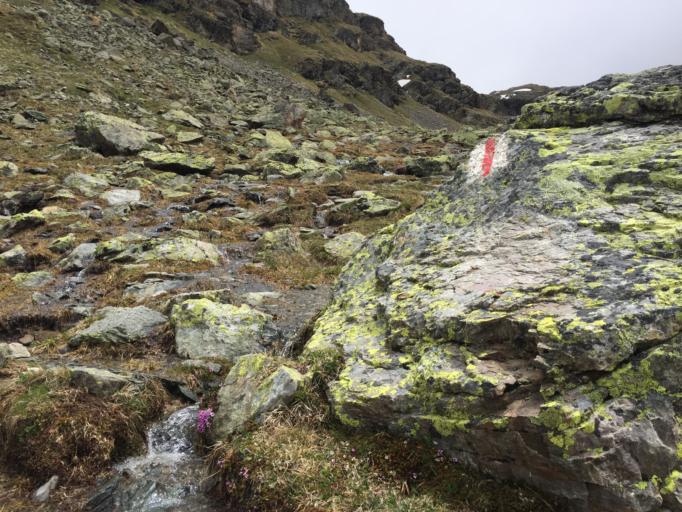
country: CH
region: Grisons
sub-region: Maloja District
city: Pontresina
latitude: 46.4786
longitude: 9.9507
